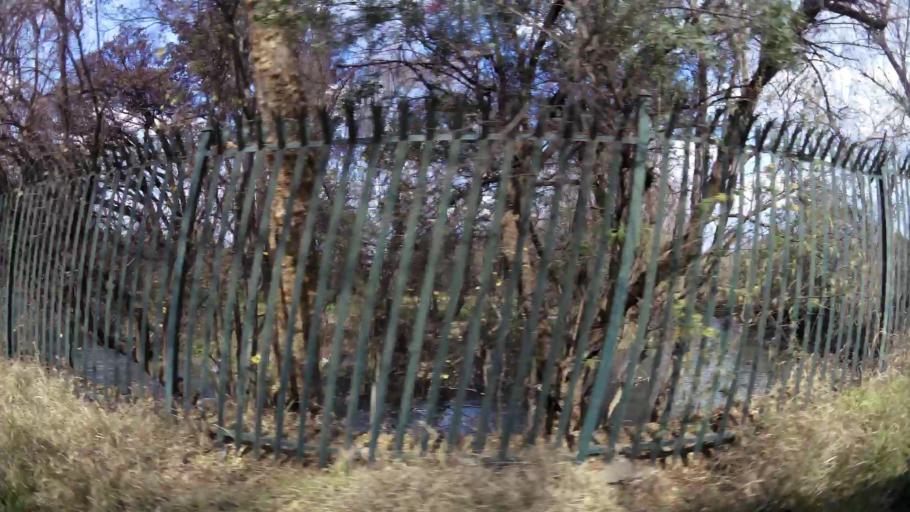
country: ZA
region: Gauteng
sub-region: City of Tshwane Metropolitan Municipality
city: Centurion
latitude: -25.8791
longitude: 28.2075
